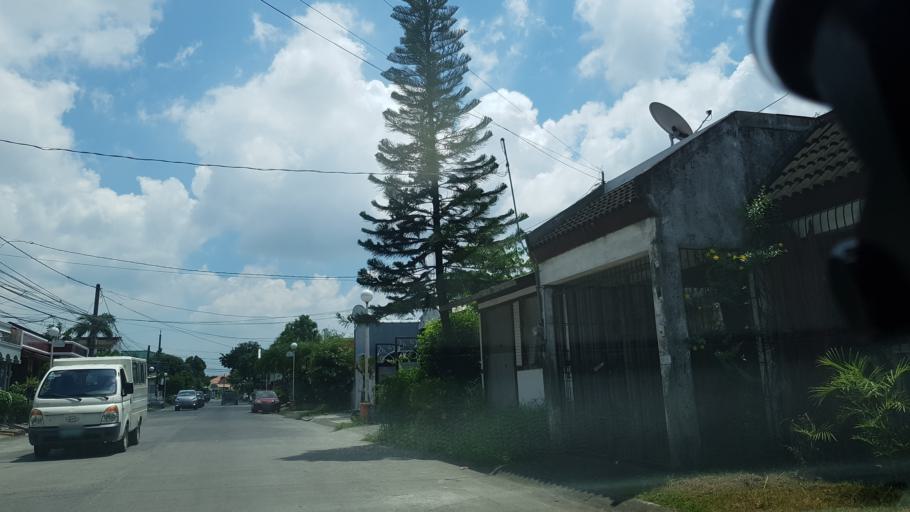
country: PH
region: Calabarzon
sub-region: Province of Rizal
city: Las Pinas
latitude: 14.4356
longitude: 120.9810
